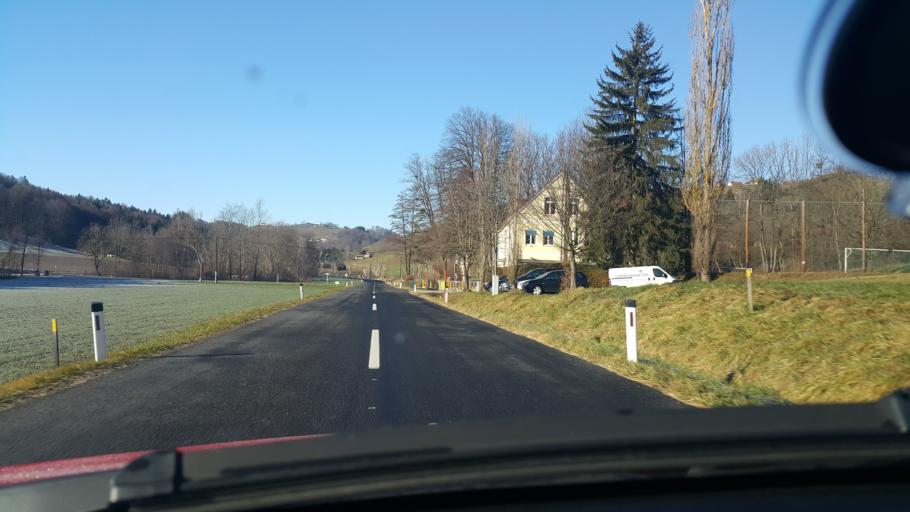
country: AT
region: Styria
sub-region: Politischer Bezirk Leibnitz
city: Sulztal an der Weinstrasse
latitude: 46.6495
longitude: 15.5445
